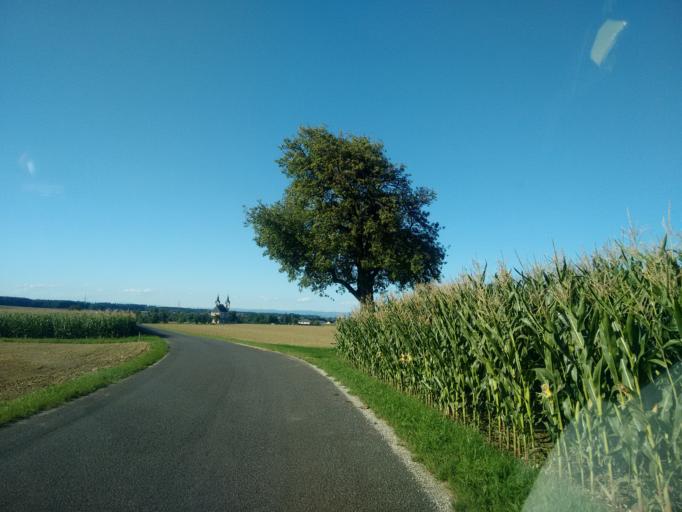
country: AT
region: Upper Austria
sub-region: Politischer Bezirk Kirchdorf an der Krems
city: Kremsmunster
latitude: 48.0698
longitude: 14.0983
